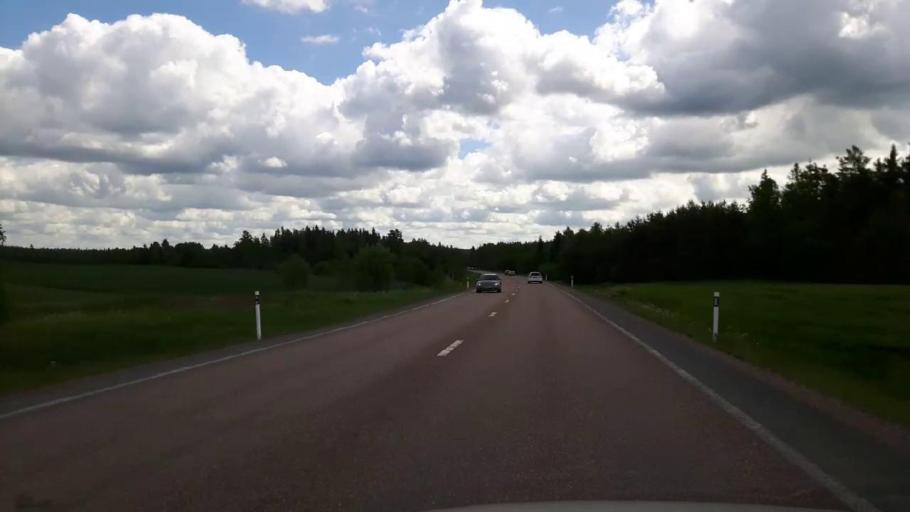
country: SE
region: Dalarna
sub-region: Saters Kommun
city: Saeter
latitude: 60.5008
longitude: 15.7460
